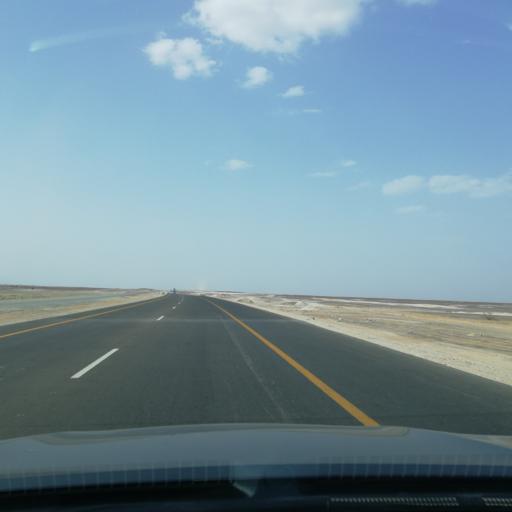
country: OM
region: Muhafazat ad Dakhiliyah
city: Adam
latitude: 22.0452
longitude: 57.5108
